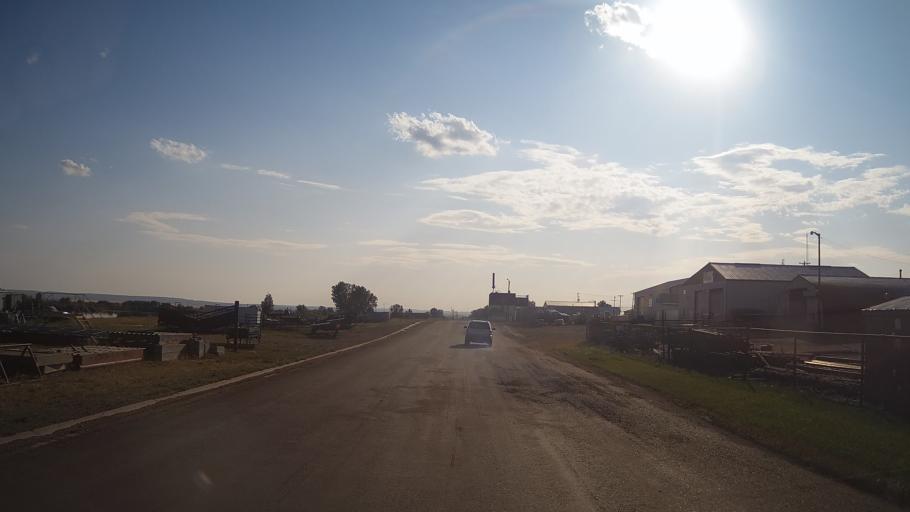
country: CA
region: Alberta
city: Hanna
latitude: 51.6427
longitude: -111.9199
